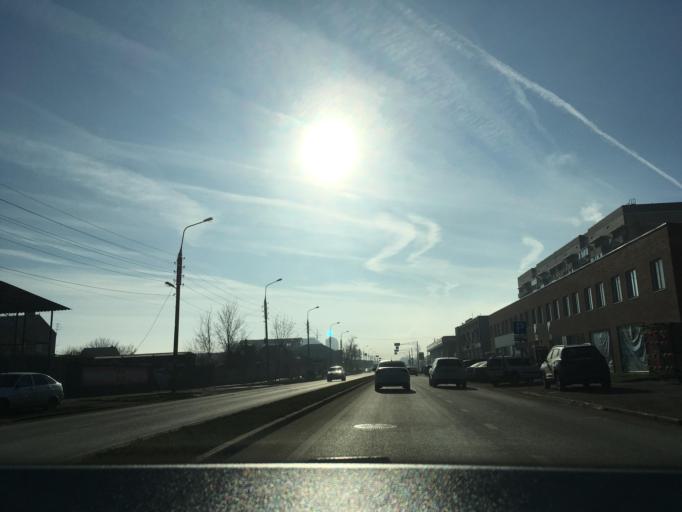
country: RU
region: Krasnodarskiy
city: Krasnodar
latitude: 45.1162
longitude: 39.0118
